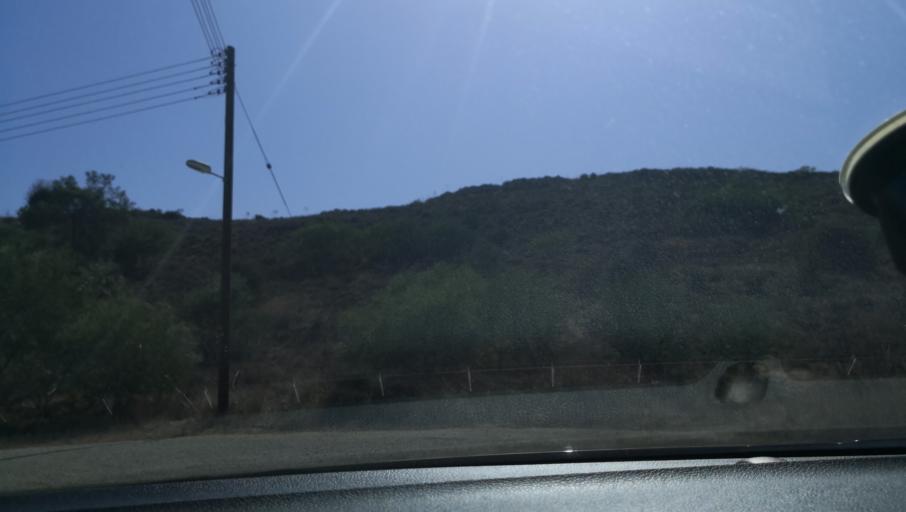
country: CY
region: Lefkosia
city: Mammari
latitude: 35.1704
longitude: 33.2065
